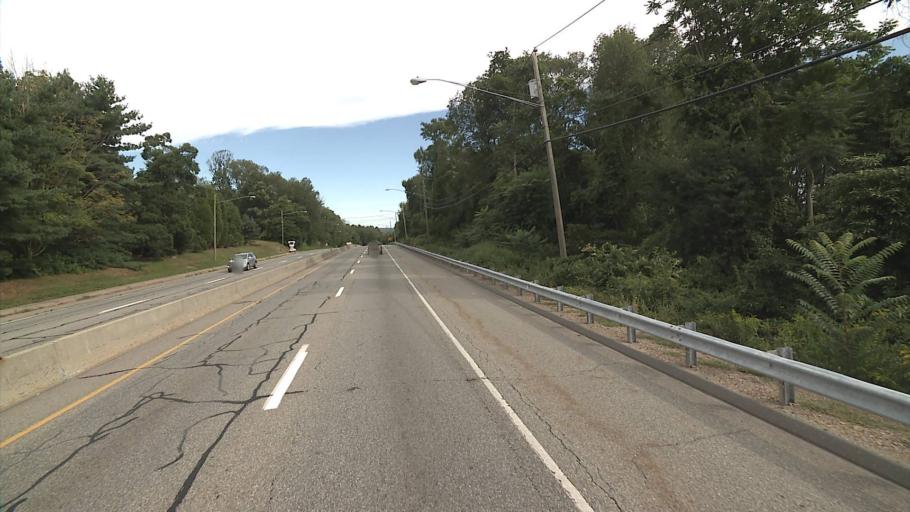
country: US
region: Connecticut
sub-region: New London County
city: New London
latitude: 41.3818
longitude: -72.1047
